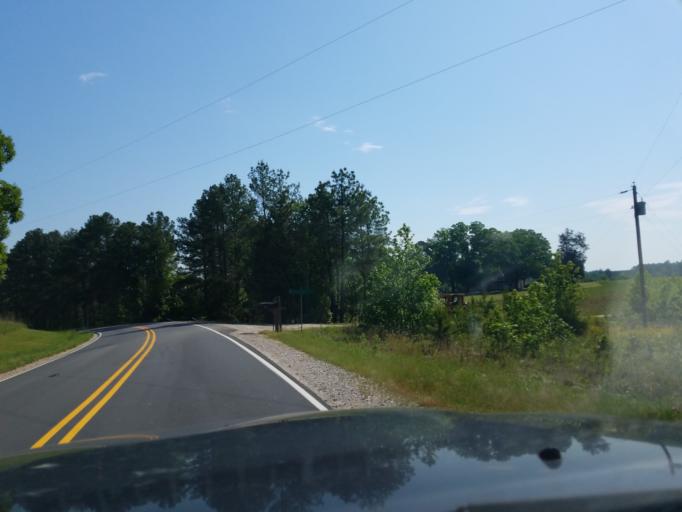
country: US
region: North Carolina
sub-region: Vance County
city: Henderson
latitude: 36.3730
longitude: -78.4468
